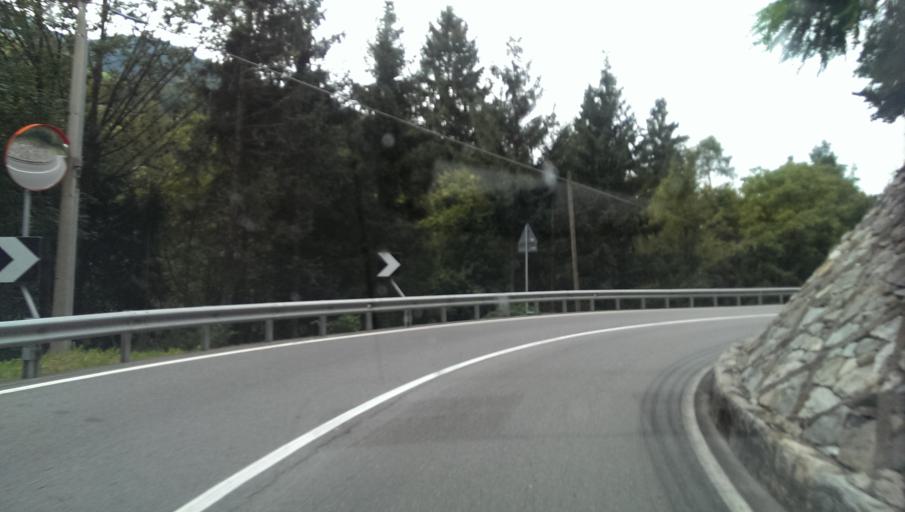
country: IT
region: Trentino-Alto Adige
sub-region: Bolzano
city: Rifiano
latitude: 46.7280
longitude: 11.1996
